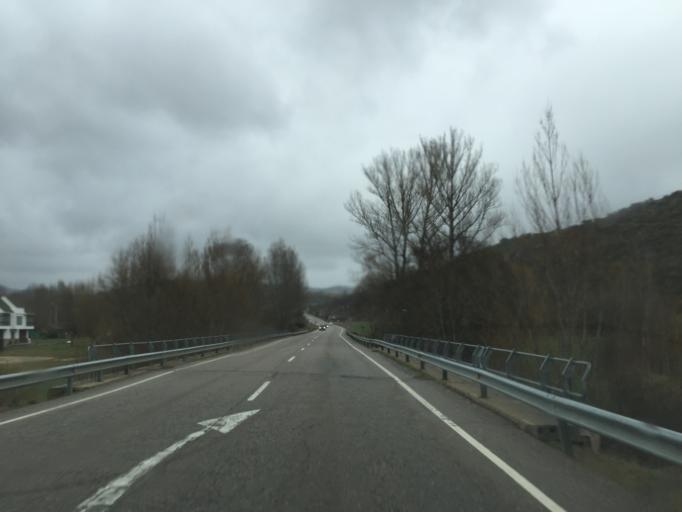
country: ES
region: Castille and Leon
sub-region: Provincia de Leon
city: Carrocera
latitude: 42.7856
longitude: -5.7652
